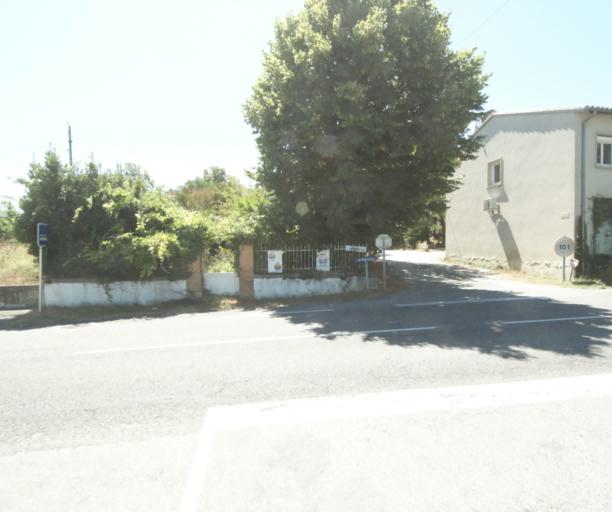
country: FR
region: Midi-Pyrenees
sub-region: Departement de la Haute-Garonne
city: Saint-Felix-Lauragais
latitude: 43.4765
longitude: 1.9289
